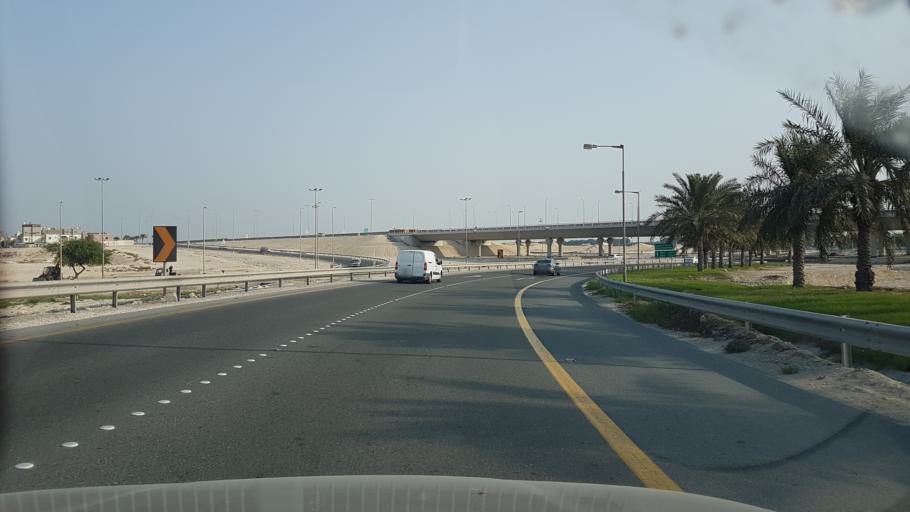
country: BH
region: Central Governorate
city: Dar Kulayb
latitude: 26.0580
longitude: 50.5163
